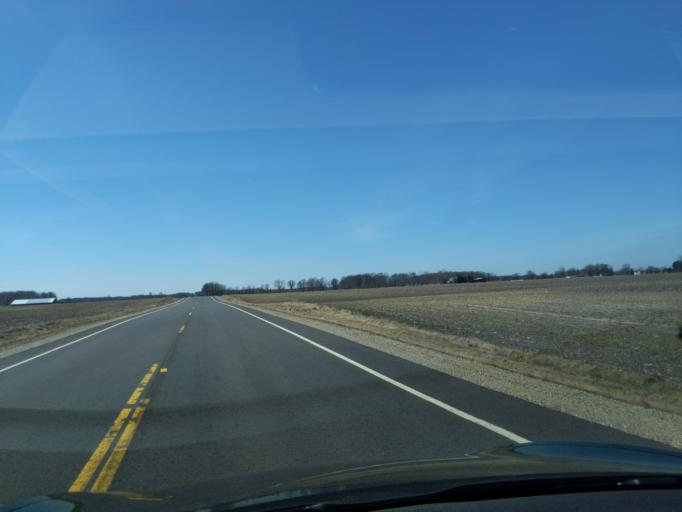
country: US
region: Michigan
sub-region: Ionia County
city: Lake Odessa
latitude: 42.7269
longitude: -85.0063
